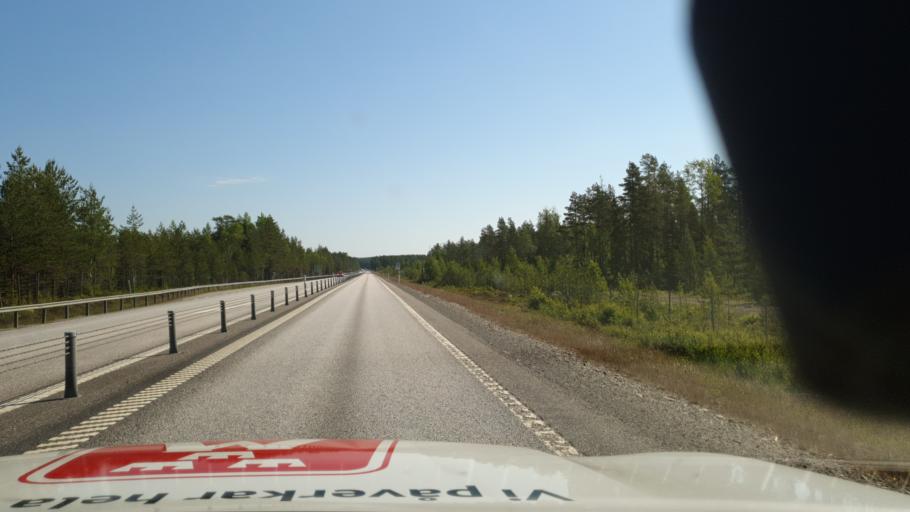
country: SE
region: Vaesterbotten
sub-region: Umea Kommun
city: Saevar
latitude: 63.9906
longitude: 20.7516
